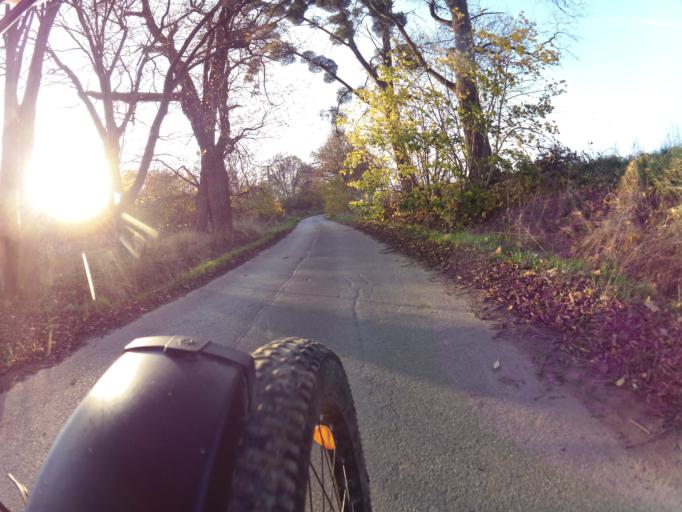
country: PL
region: Pomeranian Voivodeship
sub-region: Powiat pucki
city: Krokowa
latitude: 54.7515
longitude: 18.1866
